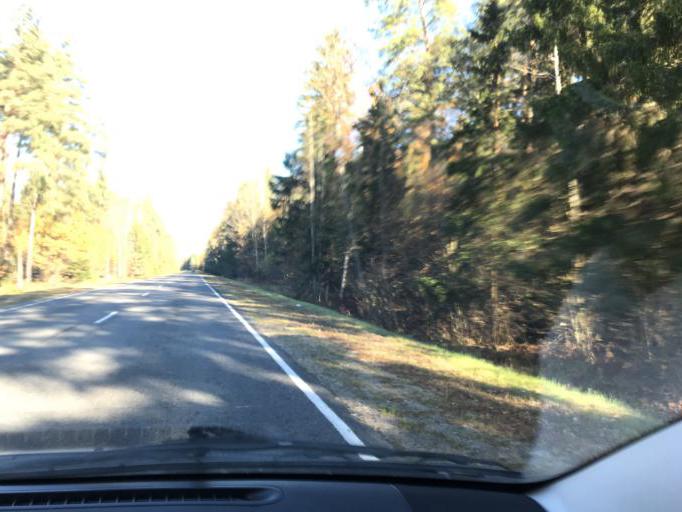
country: BY
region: Vitebsk
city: Lyepyel'
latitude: 54.9651
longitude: 28.7446
